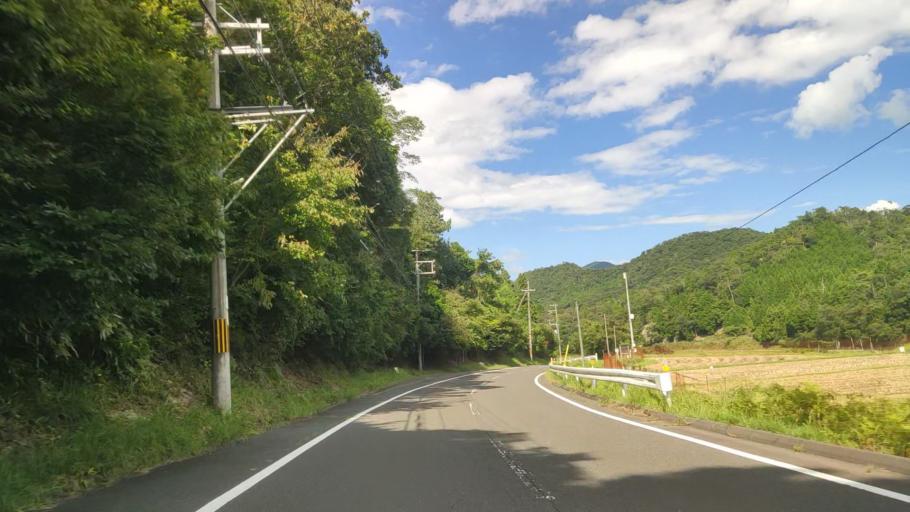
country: JP
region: Hyogo
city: Toyooka
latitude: 35.5553
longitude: 134.9778
